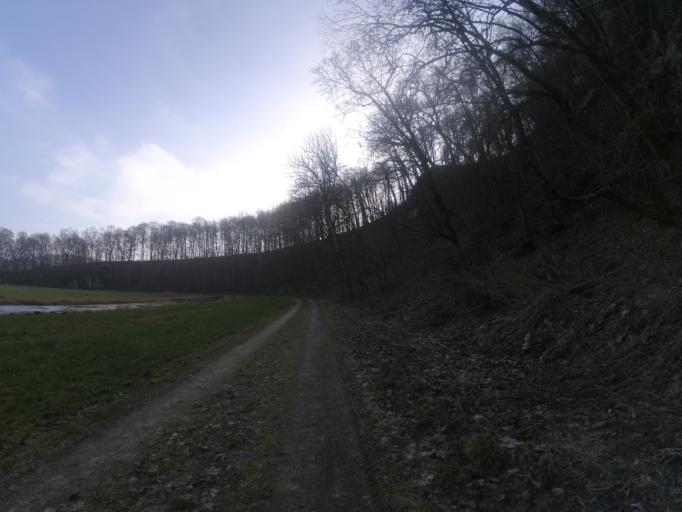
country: DE
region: Baden-Wuerttemberg
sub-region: Tuebingen Region
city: Rechtenstein
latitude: 48.2684
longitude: 9.5333
